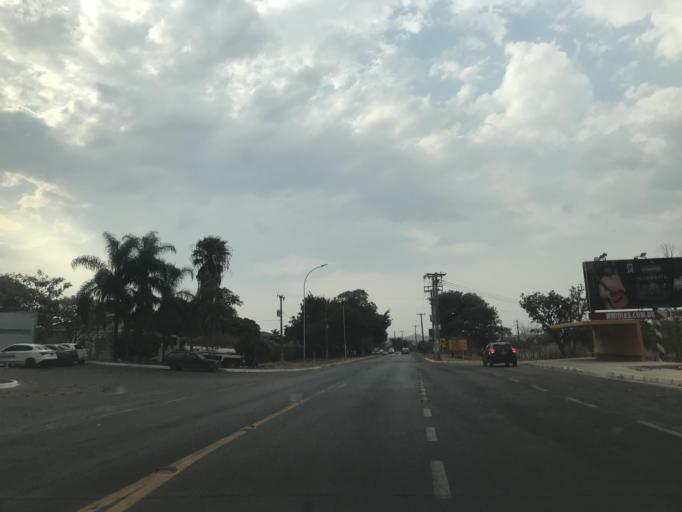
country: BR
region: Federal District
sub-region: Brasilia
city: Brasilia
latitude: -15.6694
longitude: -47.8172
